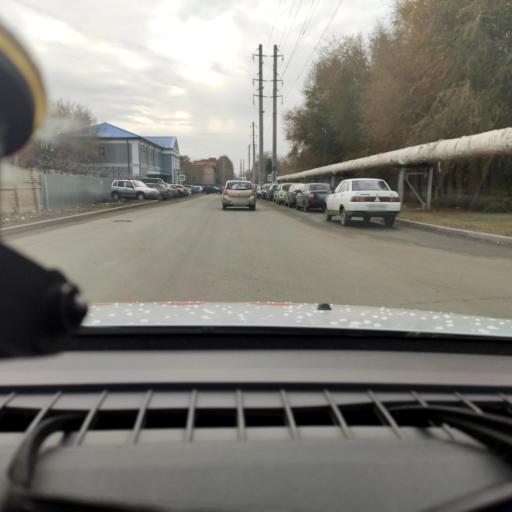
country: RU
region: Samara
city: Chapayevsk
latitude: 52.9797
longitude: 49.7198
